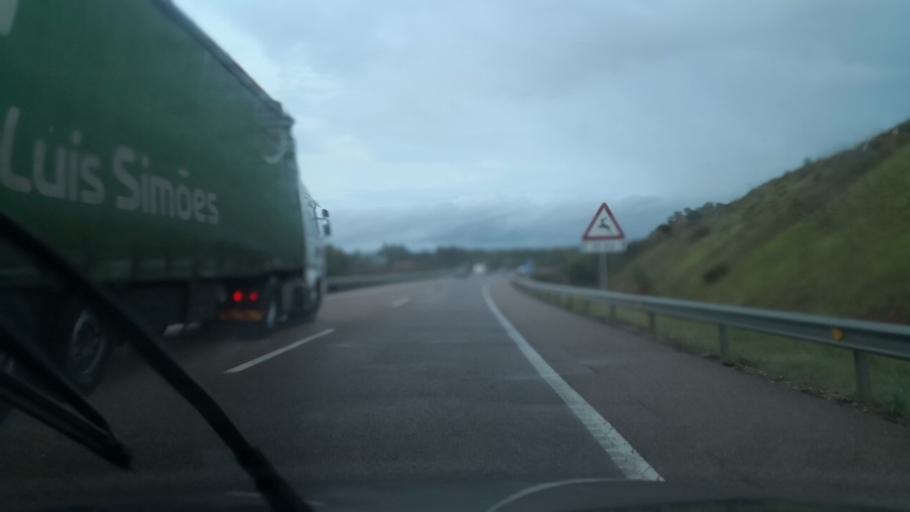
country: ES
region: Extremadura
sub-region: Provincia de Badajoz
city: Lobon
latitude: 38.8504
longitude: -6.6152
